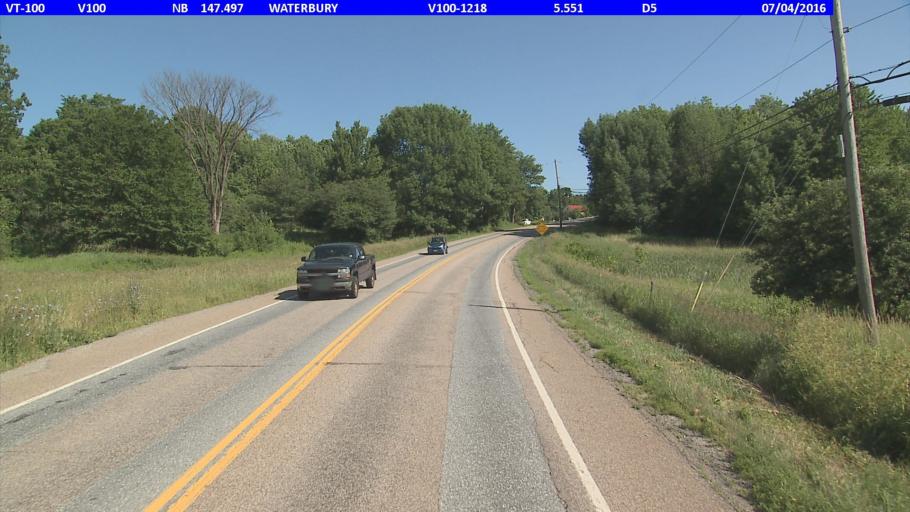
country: US
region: Vermont
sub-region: Washington County
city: Waterbury
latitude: 44.4087
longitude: -72.7217
